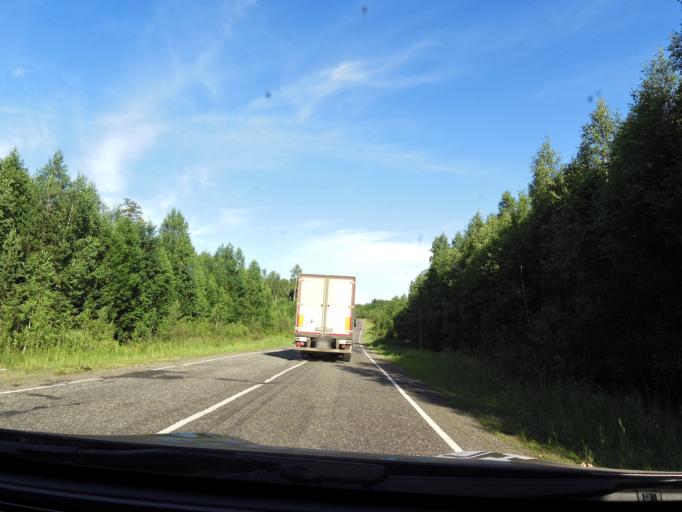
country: RU
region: Kirov
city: Chernaya Kholunitsa
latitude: 58.8758
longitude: 51.4834
